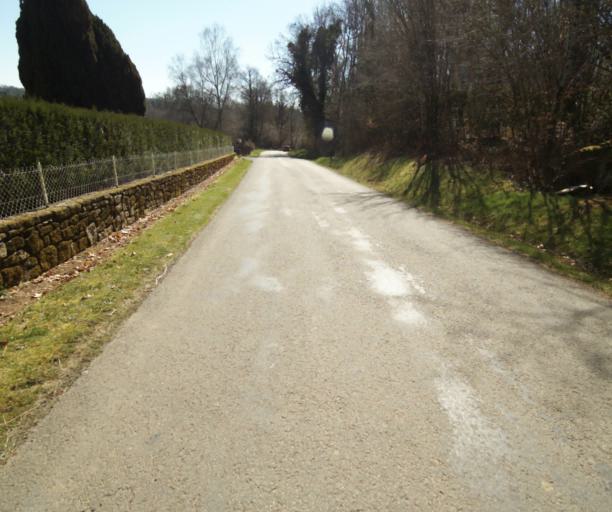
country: FR
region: Limousin
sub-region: Departement de la Correze
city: Saint-Clement
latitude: 45.3442
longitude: 1.6407
